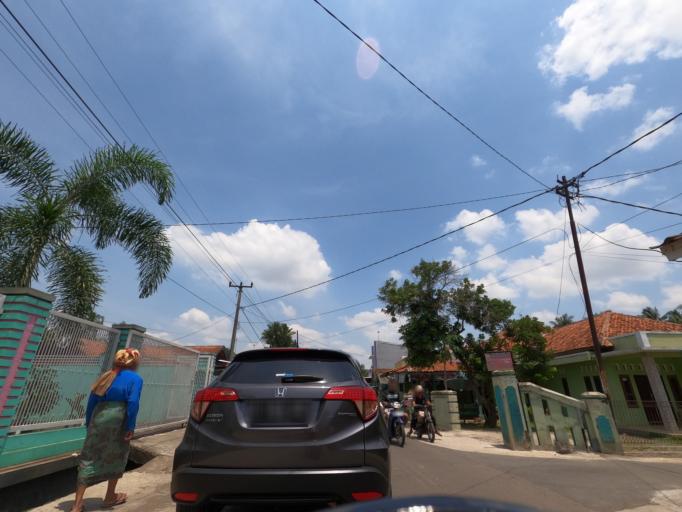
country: ID
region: West Java
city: Pamanukan
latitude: -6.5322
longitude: 107.7717
